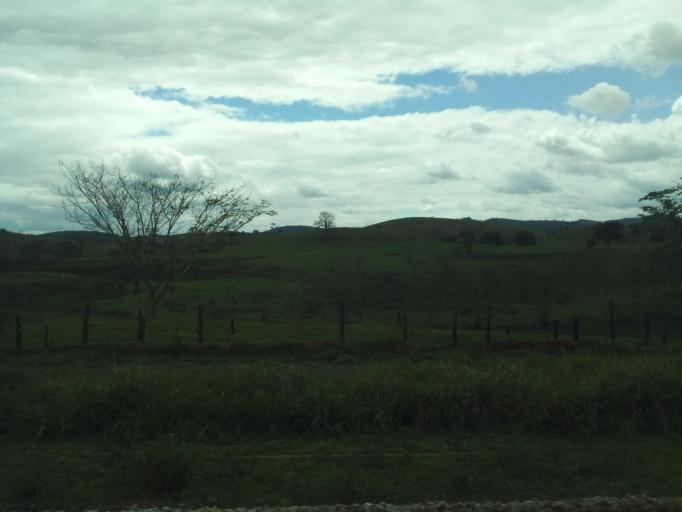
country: BR
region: Minas Gerais
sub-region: Governador Valadares
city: Governador Valadares
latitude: -19.0583
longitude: -42.1472
